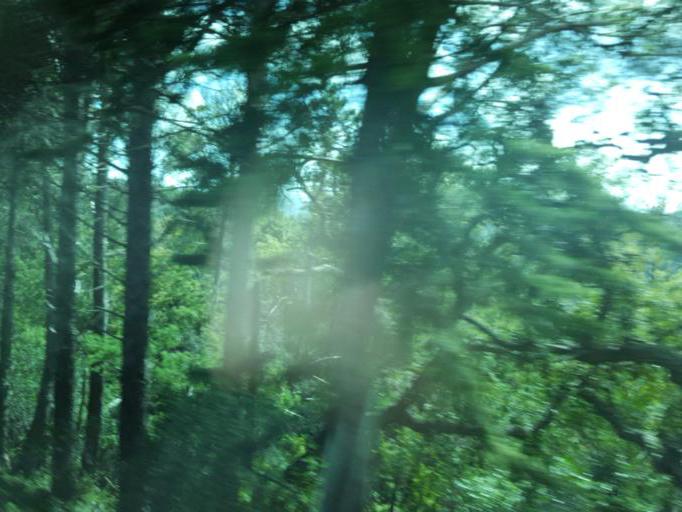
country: PT
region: Faro
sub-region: Monchique
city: Monchique
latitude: 37.2845
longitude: -8.5588
